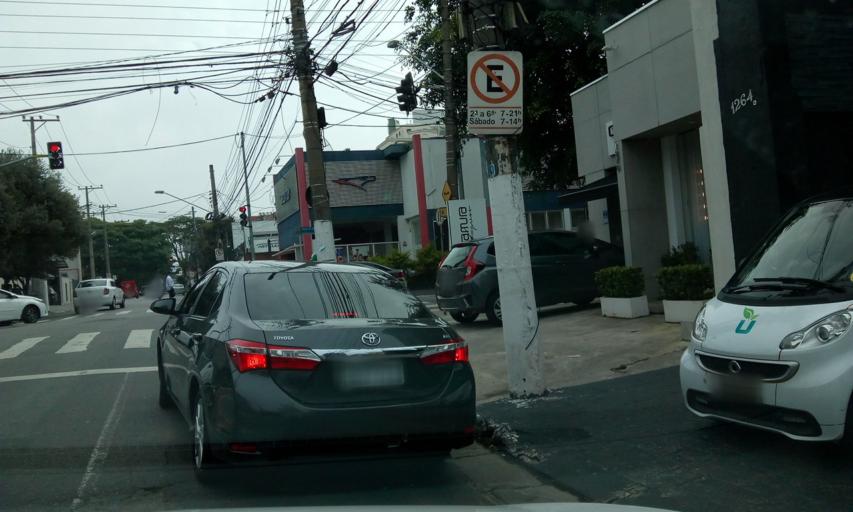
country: BR
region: Sao Paulo
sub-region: Sao Paulo
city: Sao Paulo
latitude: -23.6077
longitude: -46.6681
